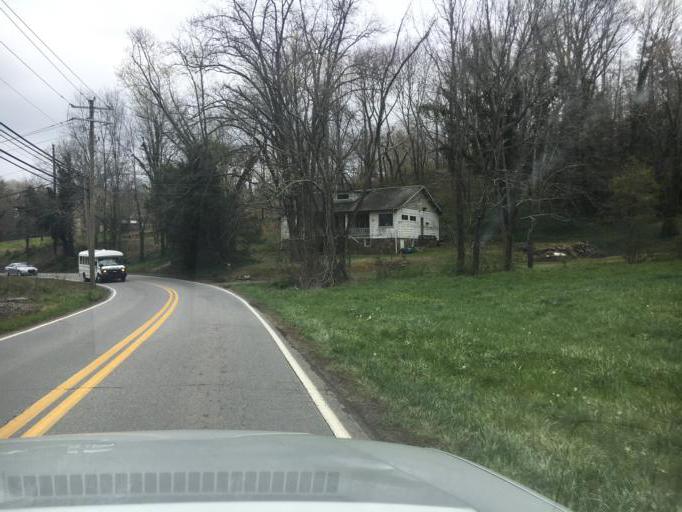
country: US
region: North Carolina
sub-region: Buncombe County
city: Woodfin
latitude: 35.6148
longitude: -82.6298
